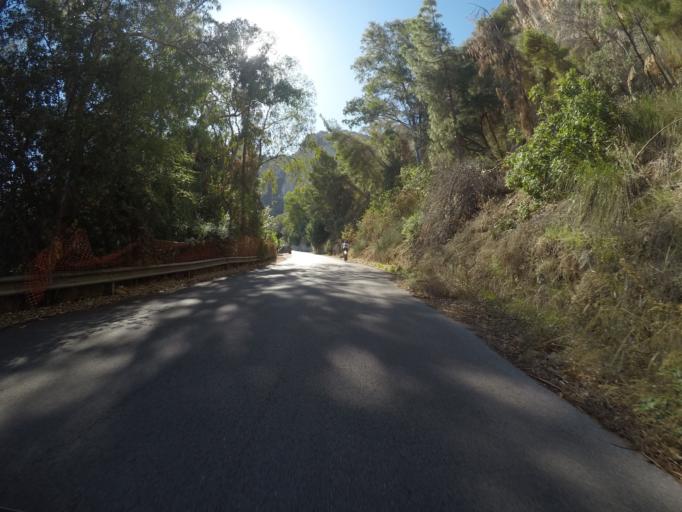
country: IT
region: Sicily
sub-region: Palermo
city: Palermo
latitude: 38.1901
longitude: 13.3398
